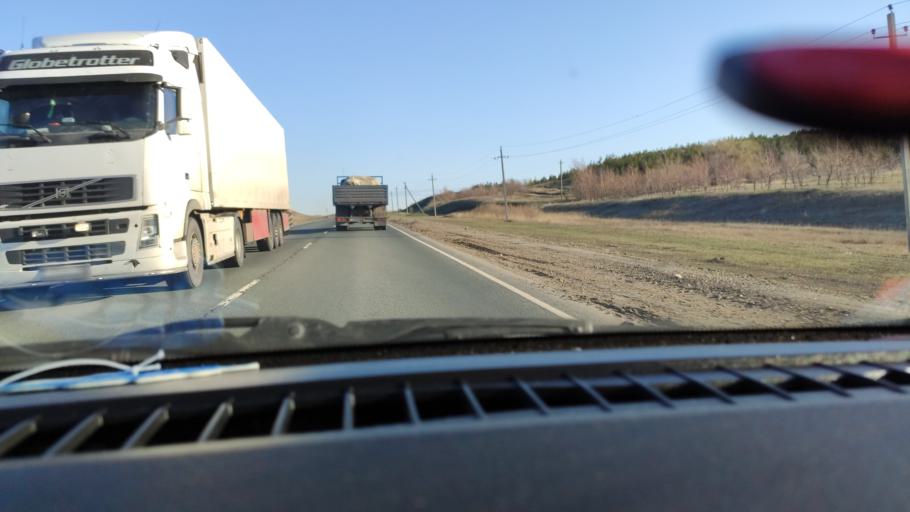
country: RU
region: Saratov
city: Alekseyevka
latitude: 52.2986
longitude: 47.9276
